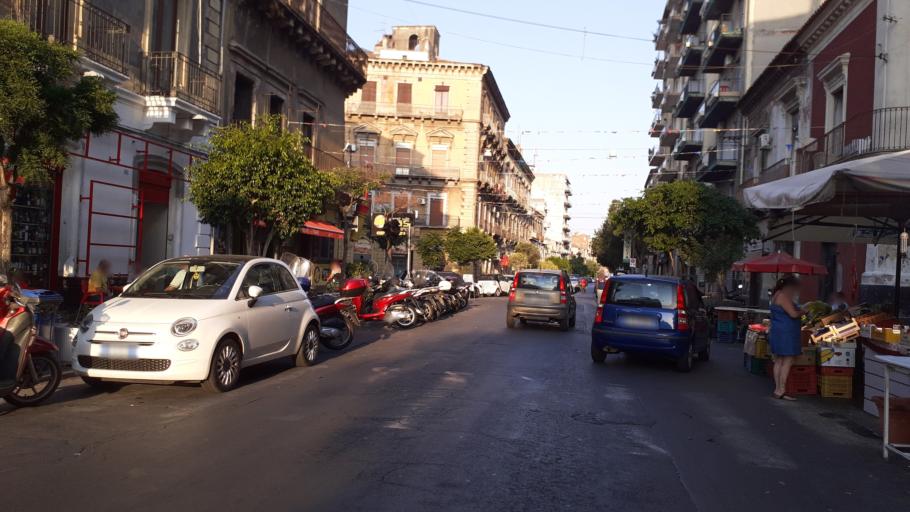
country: IT
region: Sicily
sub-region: Catania
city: Catania
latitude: 37.4988
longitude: 15.0794
